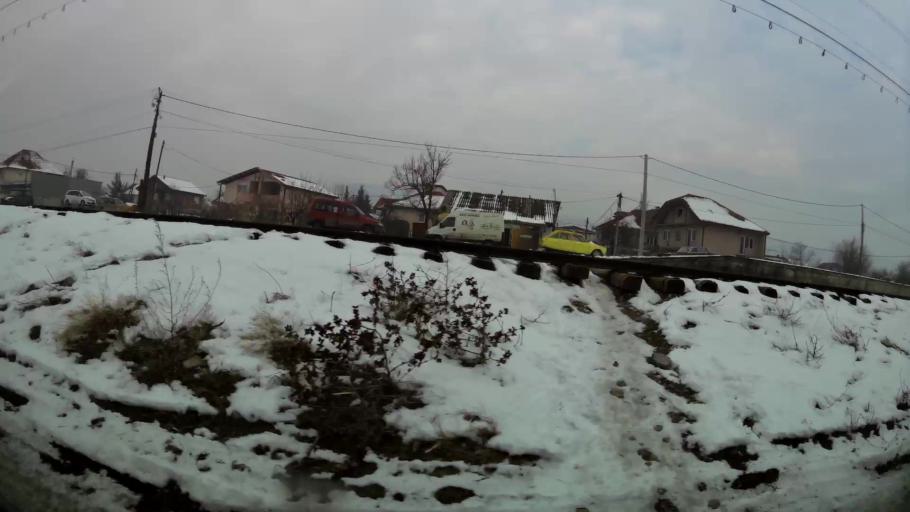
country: MK
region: Saraj
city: Saraj
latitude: 42.0454
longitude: 21.3537
